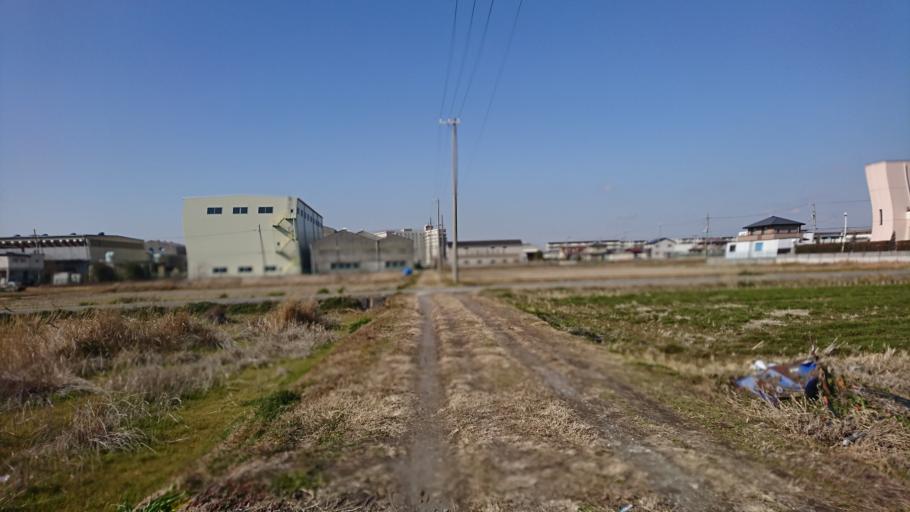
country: JP
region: Hyogo
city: Kakogawacho-honmachi
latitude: 34.7304
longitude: 134.8692
